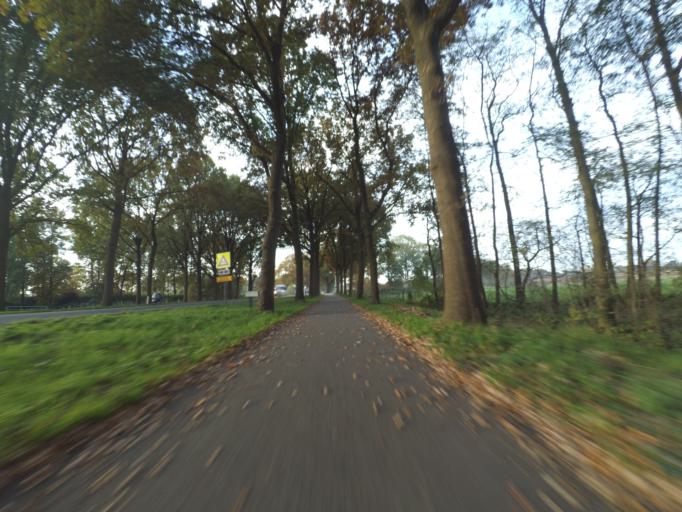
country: NL
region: Gelderland
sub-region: Gemeente Ede
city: Ederveen
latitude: 52.0582
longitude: 5.5603
